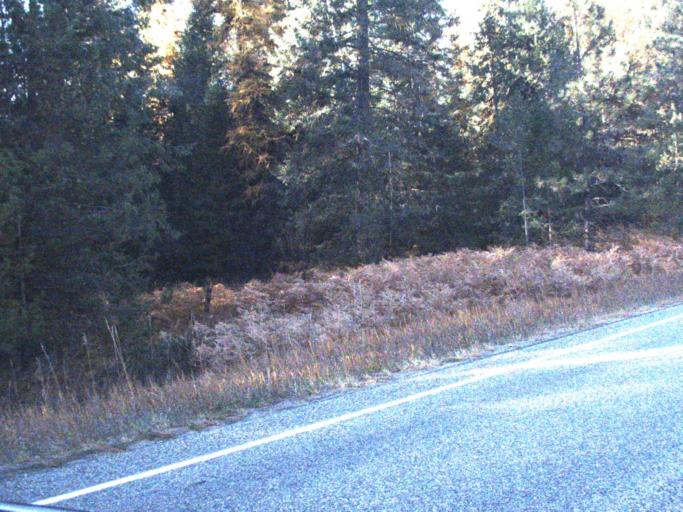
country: CA
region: British Columbia
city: Rossland
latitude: 48.9353
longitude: -117.7726
